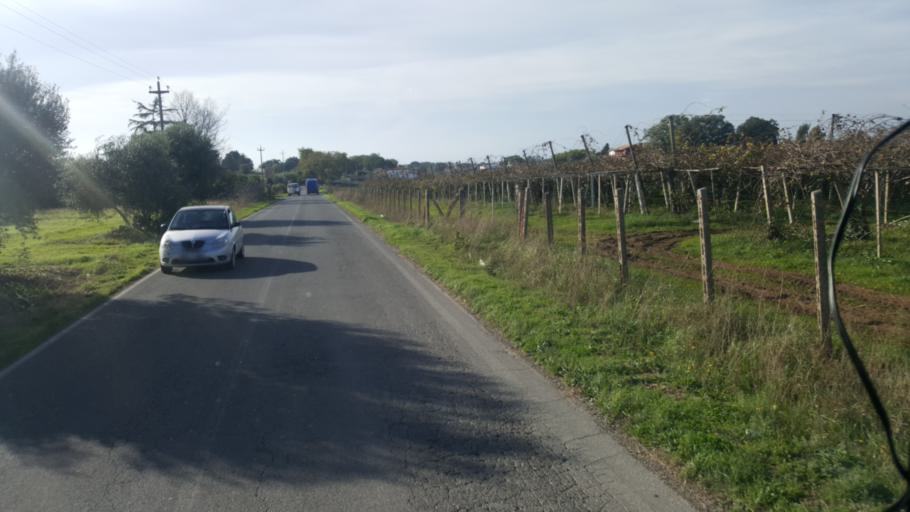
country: IT
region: Latium
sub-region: Provincia di Latina
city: Casalazzara
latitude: 41.6309
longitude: 12.6012
